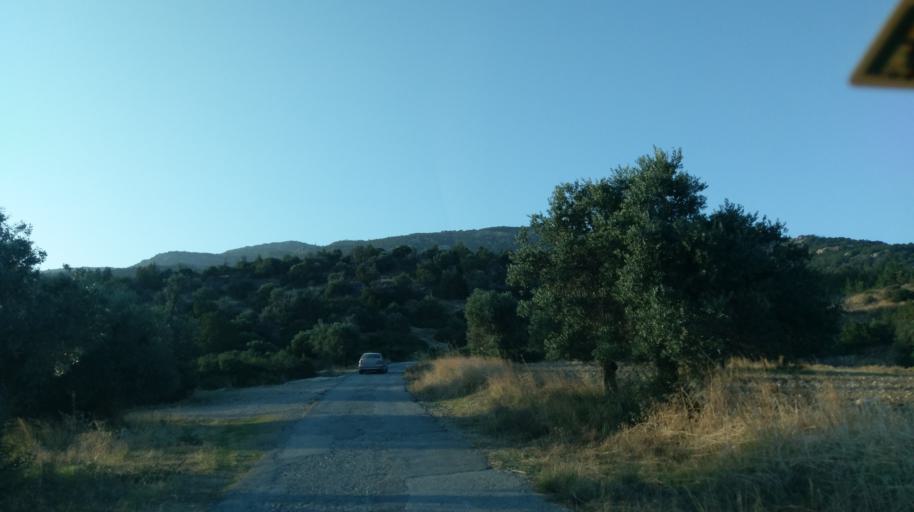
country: CY
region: Ammochostos
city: Trikomo
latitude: 35.3704
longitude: 33.9048
